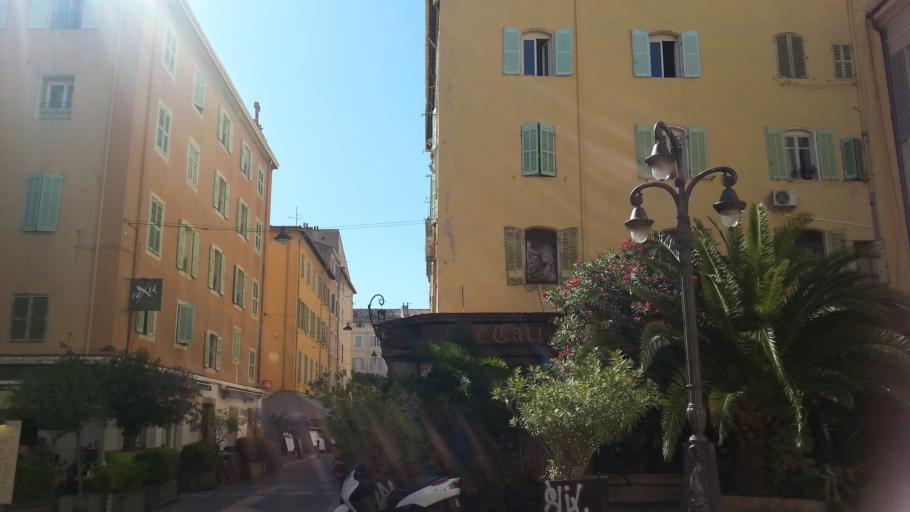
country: FR
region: Provence-Alpes-Cote d'Azur
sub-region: Departement des Bouches-du-Rhone
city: Marseille 02
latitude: 43.2933
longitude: 5.3732
